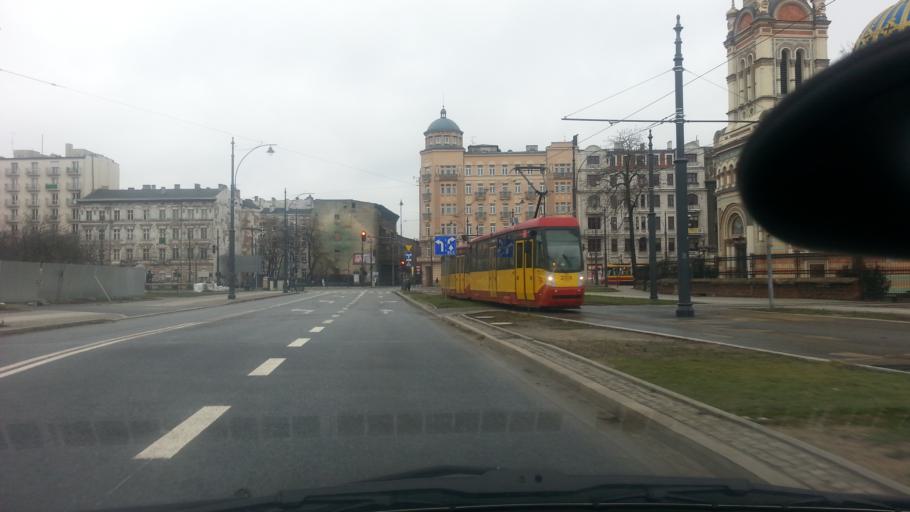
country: PL
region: Lodz Voivodeship
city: Lodz
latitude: 51.7702
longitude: 19.4639
